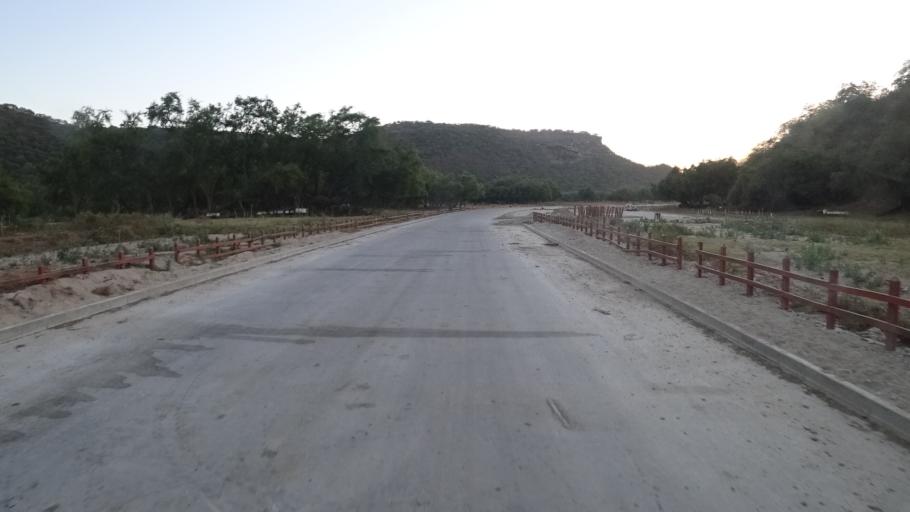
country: OM
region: Zufar
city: Salalah
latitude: 17.0923
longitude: 54.4466
